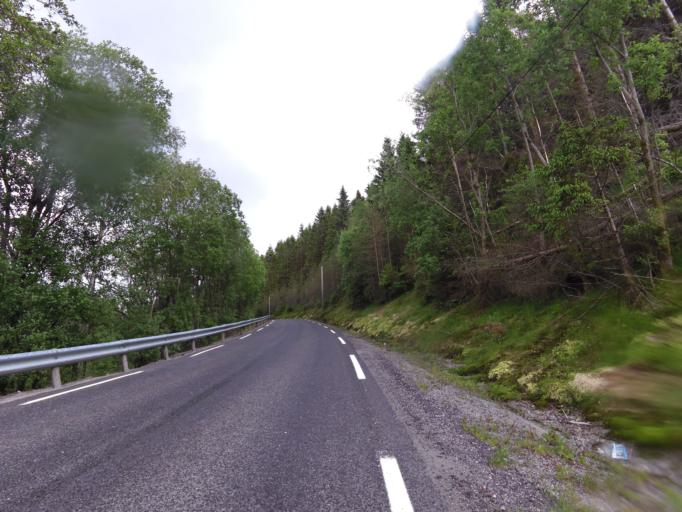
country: NO
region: Vest-Agder
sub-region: Lyngdal
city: Lyngdal
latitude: 58.1149
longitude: 7.0699
